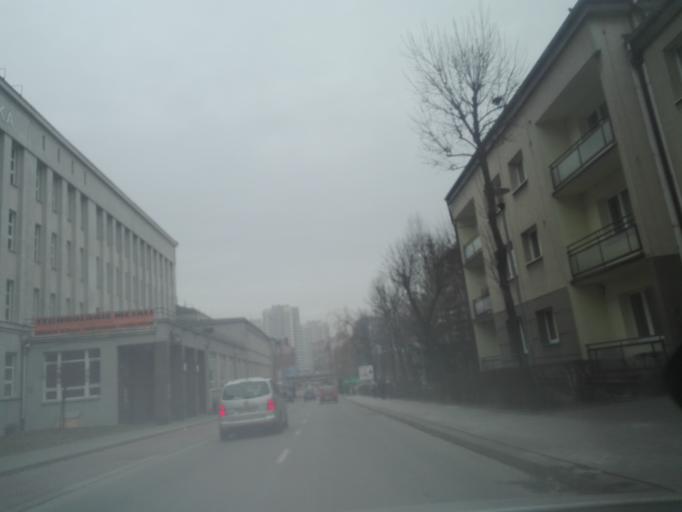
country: PL
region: Silesian Voivodeship
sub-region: Katowice
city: Katowice
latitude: 50.2554
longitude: 19.0352
